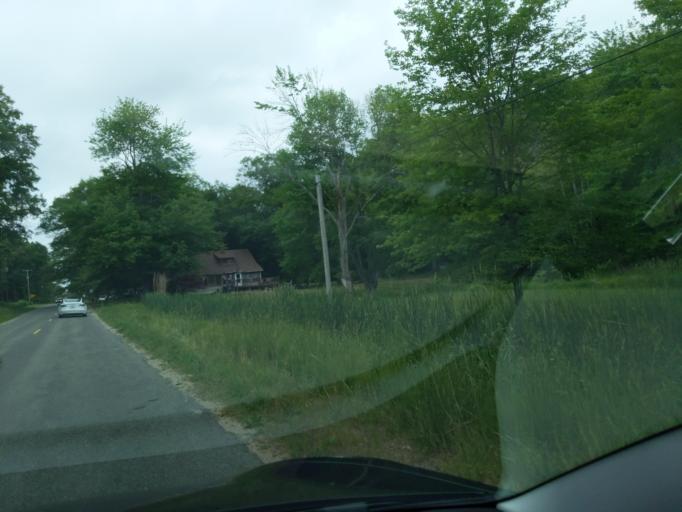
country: US
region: Michigan
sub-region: Muskegon County
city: North Muskegon
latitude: 43.2505
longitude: -86.3223
